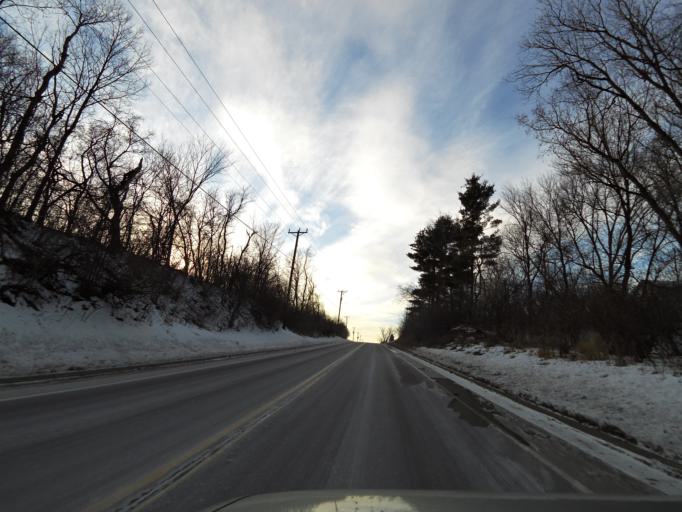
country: US
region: Minnesota
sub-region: Washington County
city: Afton
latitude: 44.8911
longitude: -92.8197
